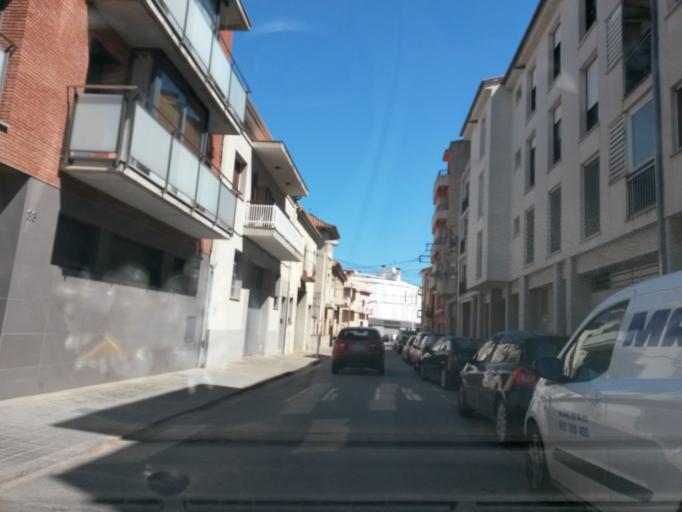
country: ES
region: Catalonia
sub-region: Provincia de Girona
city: Banyoles
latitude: 42.1170
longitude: 2.7596
